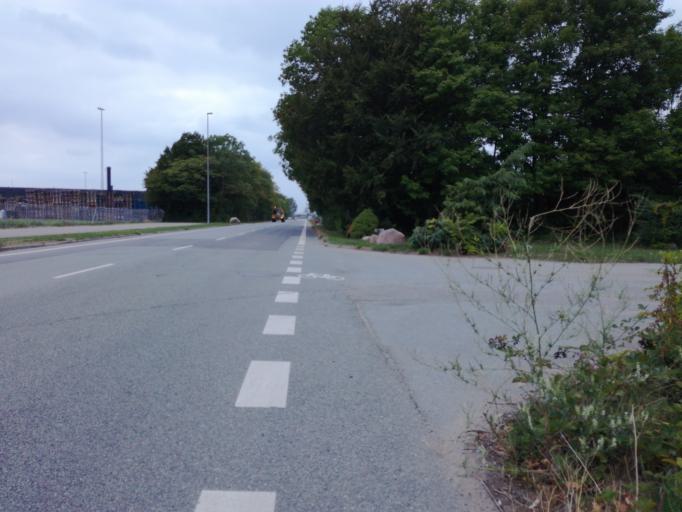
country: DK
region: South Denmark
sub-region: Fredericia Kommune
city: Fredericia
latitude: 55.5930
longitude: 9.7645
